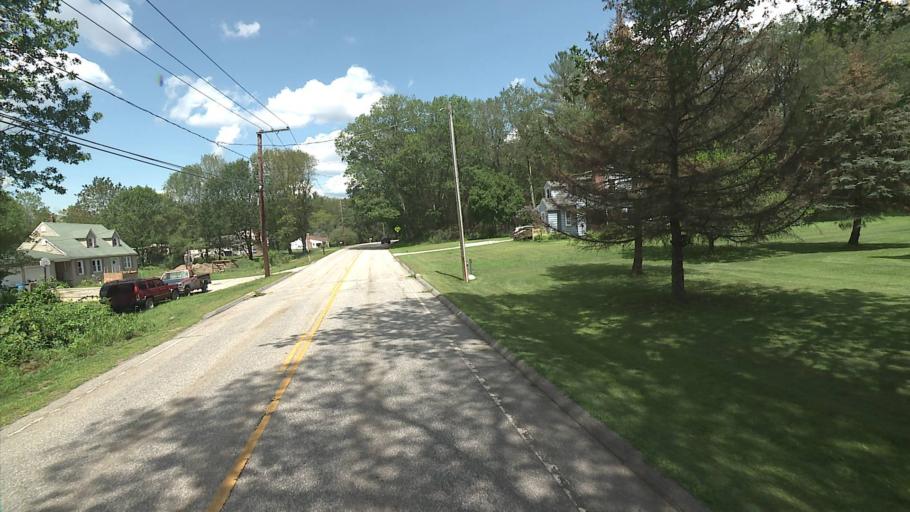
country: US
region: Connecticut
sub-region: Windham County
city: Windham
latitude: 41.7320
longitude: -72.1649
